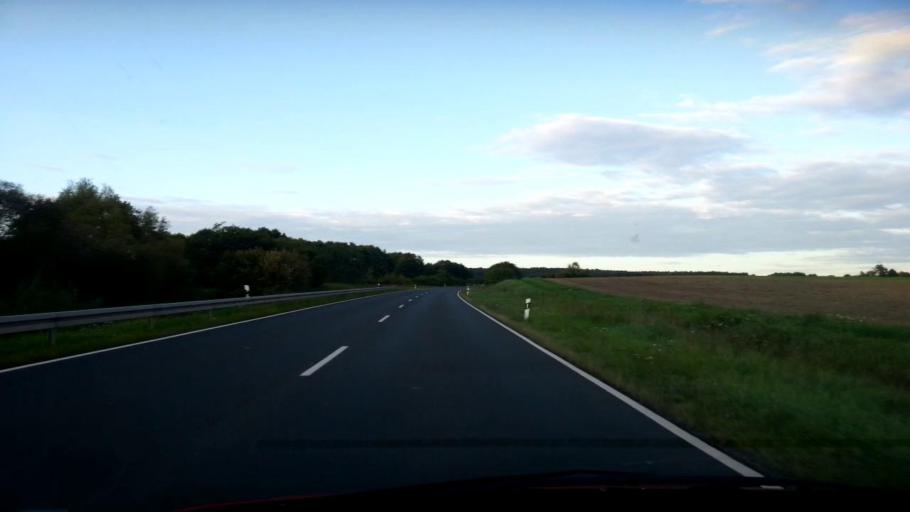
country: DE
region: Bavaria
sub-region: Upper Franconia
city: Walsdorf
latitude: 49.8301
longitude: 10.7928
